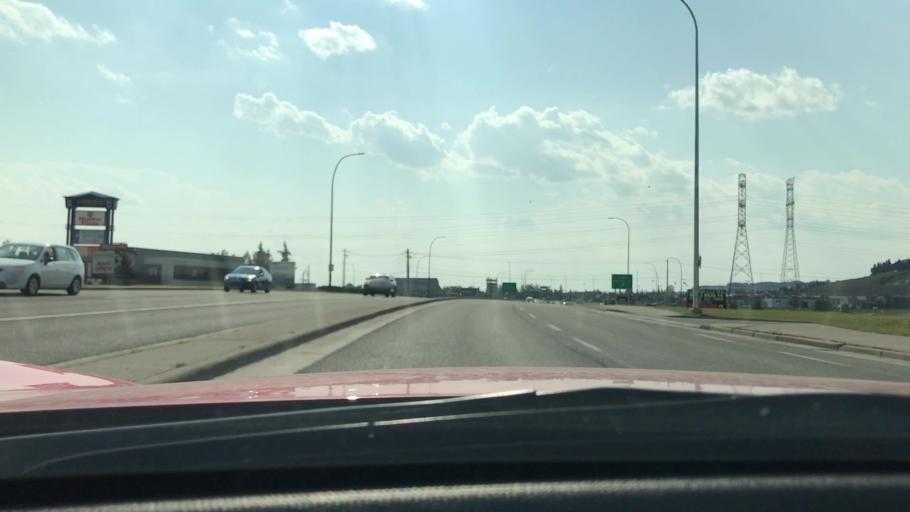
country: CA
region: Alberta
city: Calgary
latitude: 51.0179
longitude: -114.1609
